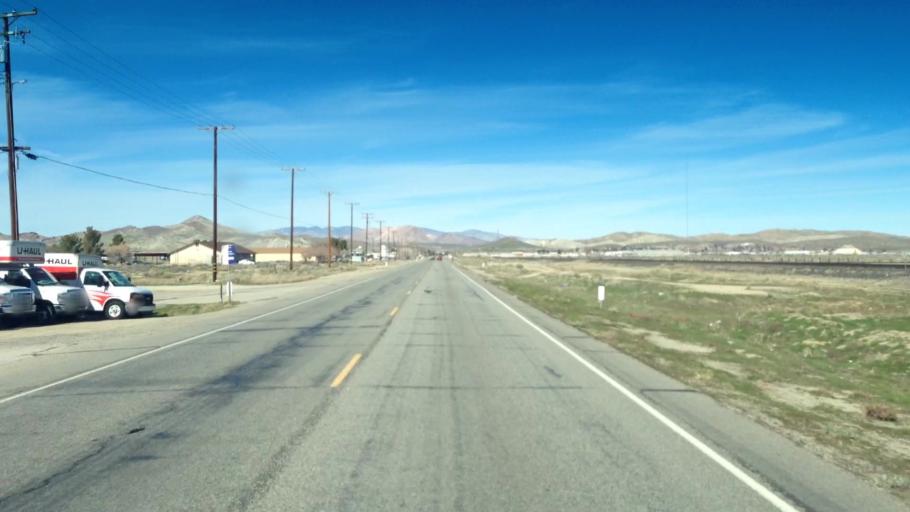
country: US
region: California
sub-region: Kern County
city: Rosamond
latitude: 34.8383
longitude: -118.1588
